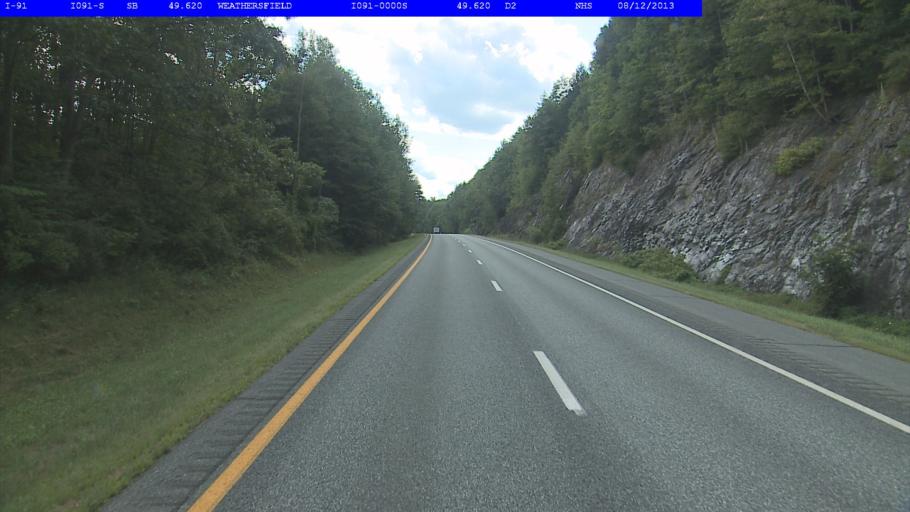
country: US
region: New Hampshire
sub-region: Sullivan County
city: Claremont
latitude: 43.3781
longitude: -72.4221
